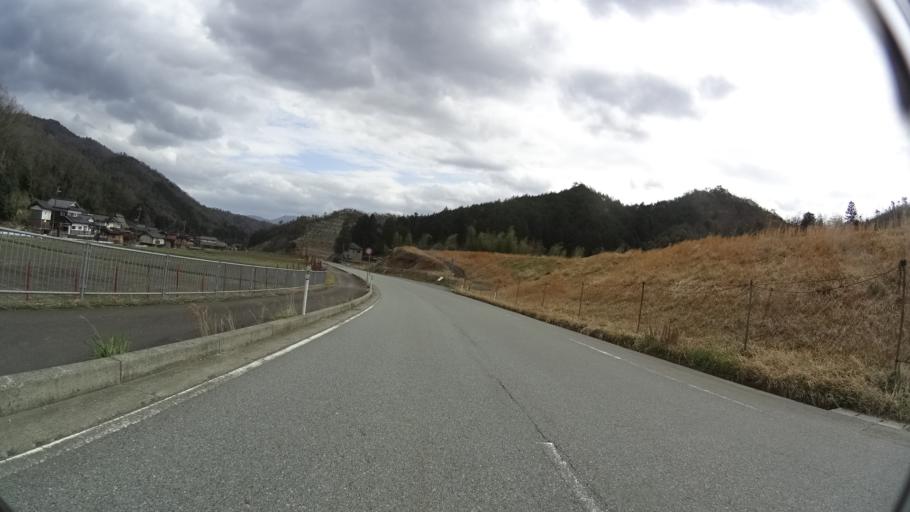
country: JP
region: Hyogo
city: Toyooka
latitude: 35.4869
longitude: 134.9226
